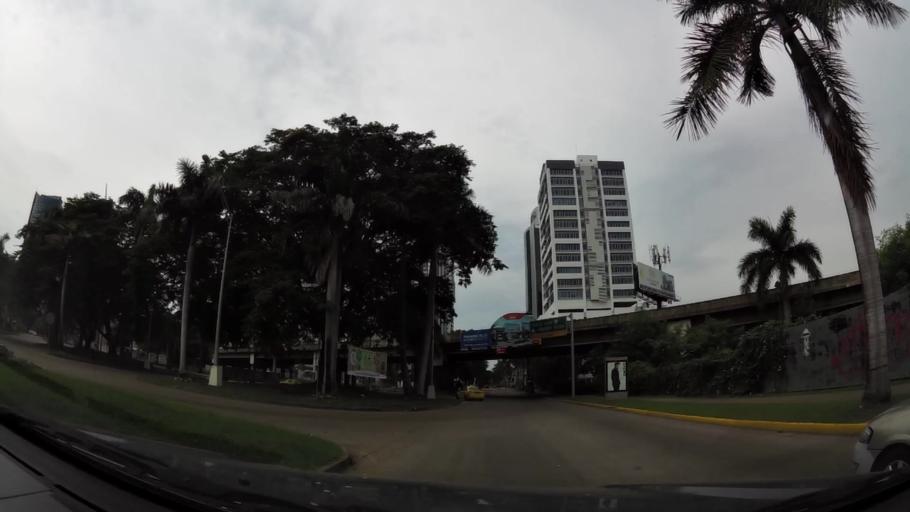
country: PA
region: Panama
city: San Miguelito
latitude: 9.0156
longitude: -79.4748
